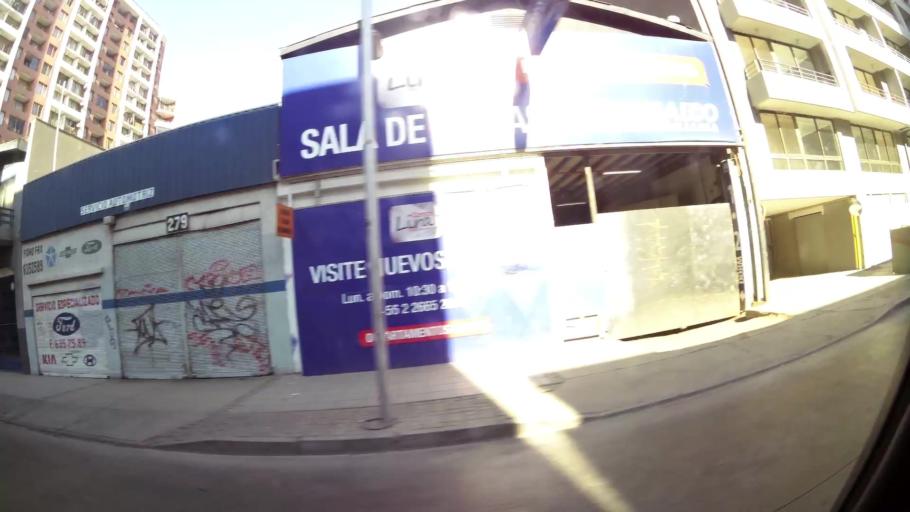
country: CL
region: Santiago Metropolitan
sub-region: Provincia de Santiago
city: Santiago
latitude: -33.4467
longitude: -70.6400
